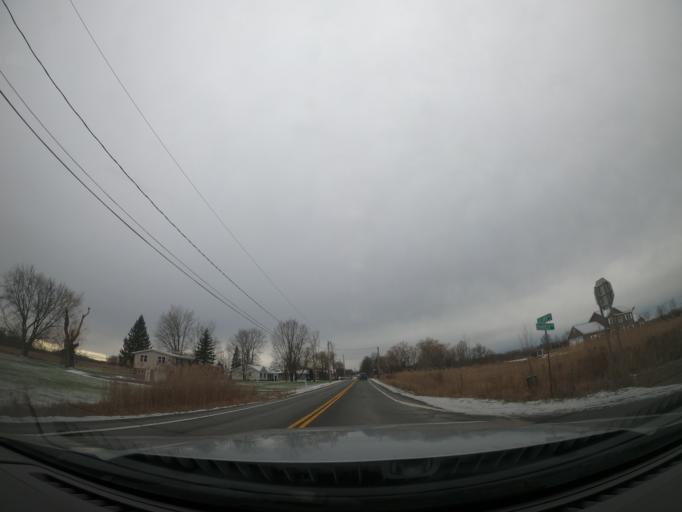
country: US
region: New York
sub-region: Onondaga County
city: Minoa
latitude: 43.1142
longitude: -76.0133
